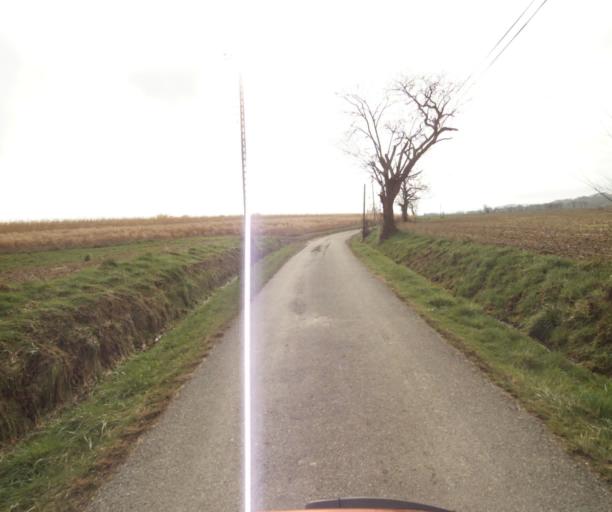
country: FR
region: Midi-Pyrenees
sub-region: Departement de l'Ariege
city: Mazeres
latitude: 43.1883
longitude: 1.6619
